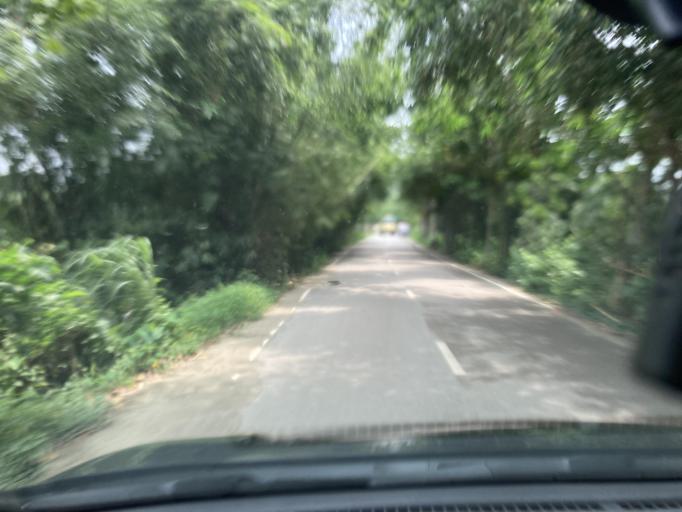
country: BD
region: Dhaka
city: Dohar
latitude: 23.7690
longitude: 90.1977
